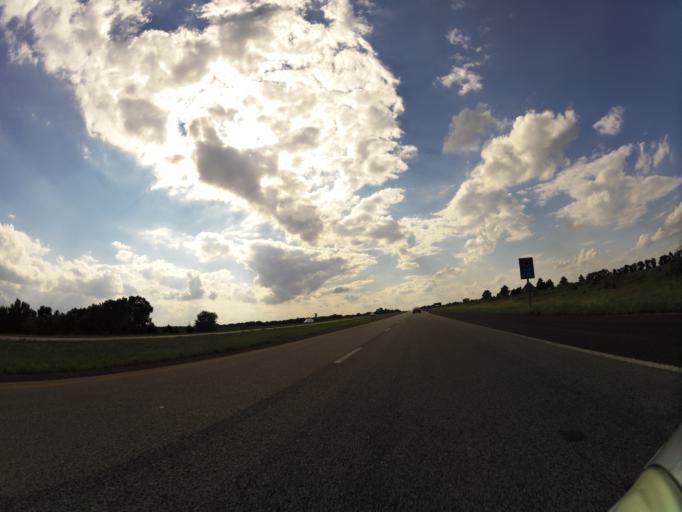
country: US
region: Kansas
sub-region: Reno County
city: Haven
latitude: 37.9233
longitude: -97.8360
